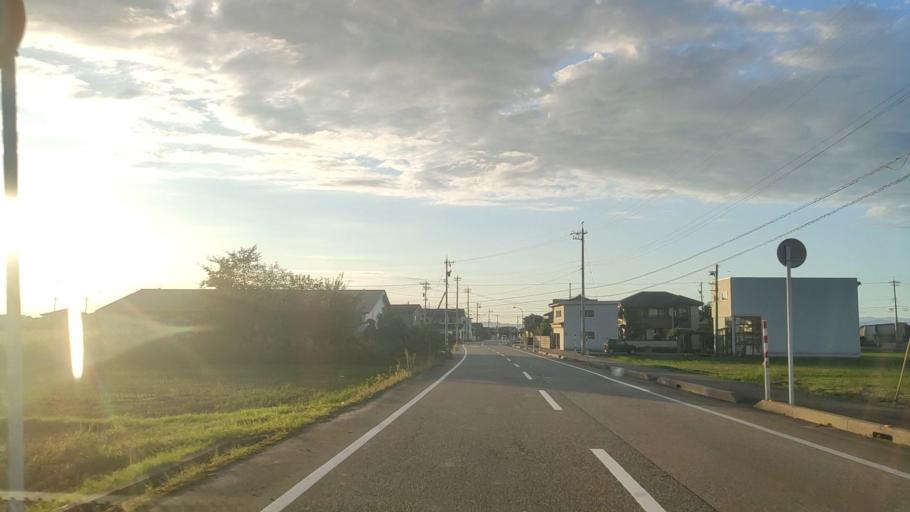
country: JP
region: Toyama
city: Nanto-shi
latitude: 36.5961
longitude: 136.9481
